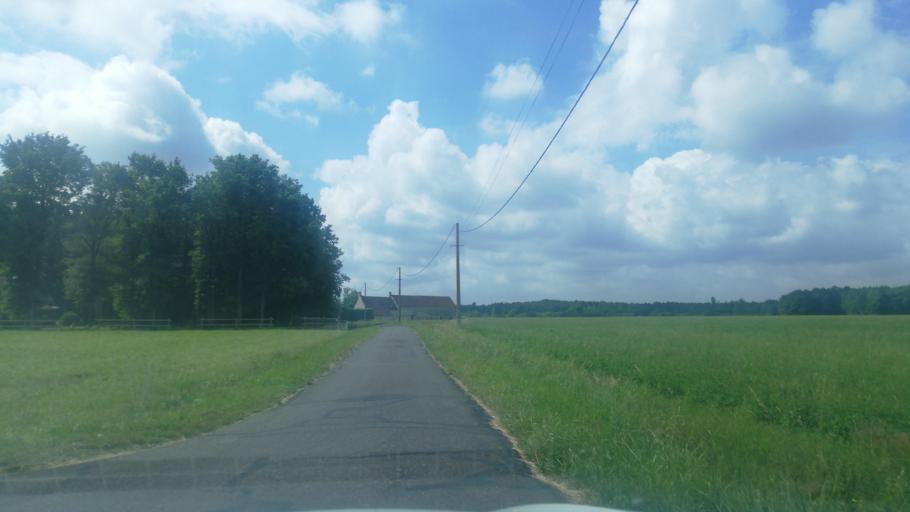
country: FR
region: Centre
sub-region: Departement du Loir-et-Cher
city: Saint-Romain-sur-Cher
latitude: 47.3564
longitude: 1.3932
